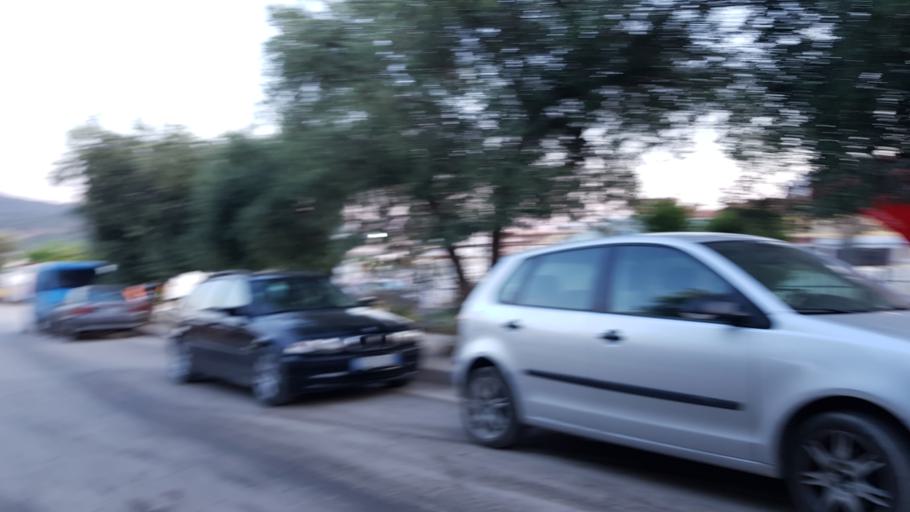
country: AL
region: Vlore
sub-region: Rrethi i Sarandes
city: Xarre
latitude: 39.7708
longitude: 20.0032
